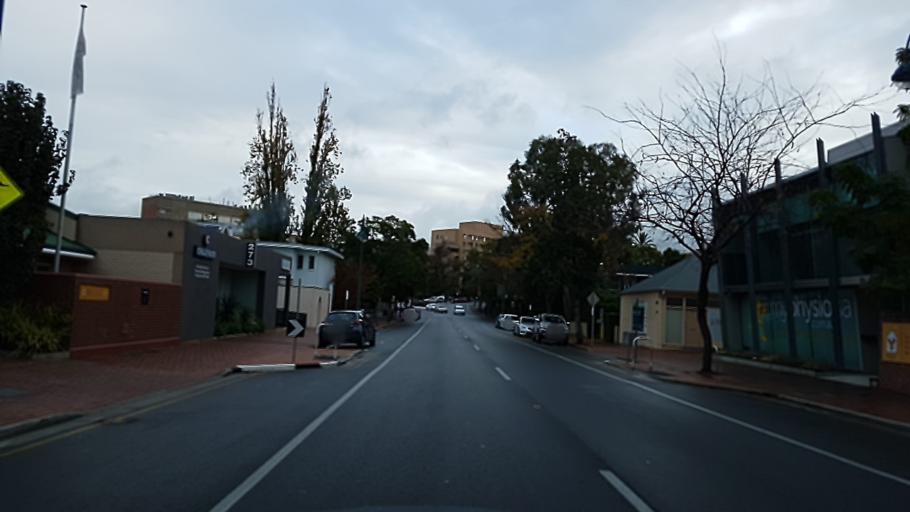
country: AU
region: South Australia
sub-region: Adelaide
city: North Adelaide
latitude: -34.9096
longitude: 138.6026
